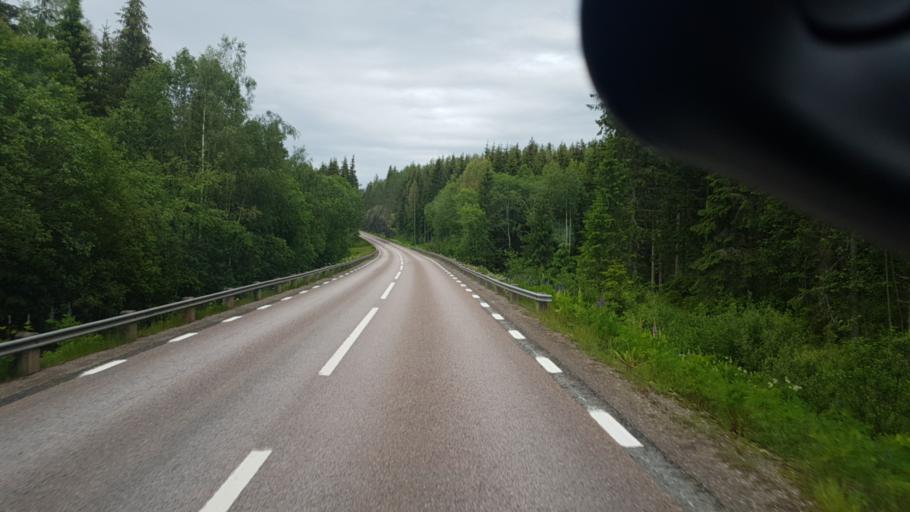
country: SE
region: Vaermland
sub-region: Eda Kommun
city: Amotfors
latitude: 59.7301
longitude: 12.2268
